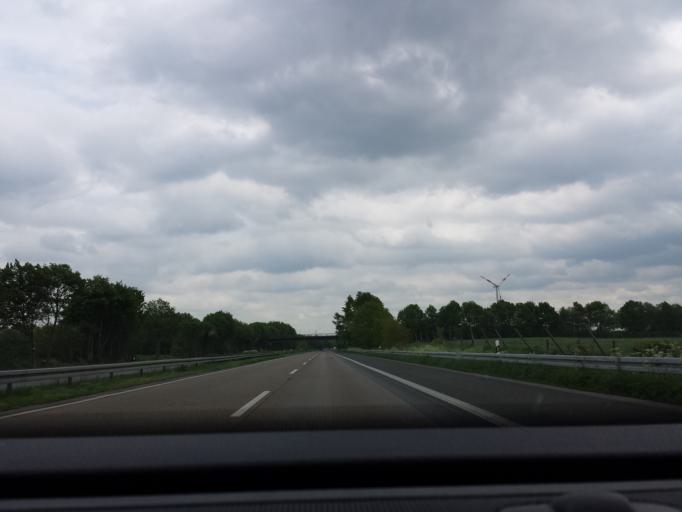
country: DE
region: North Rhine-Westphalia
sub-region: Regierungsbezirk Munster
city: Isselburg
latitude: 51.8222
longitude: 6.4136
